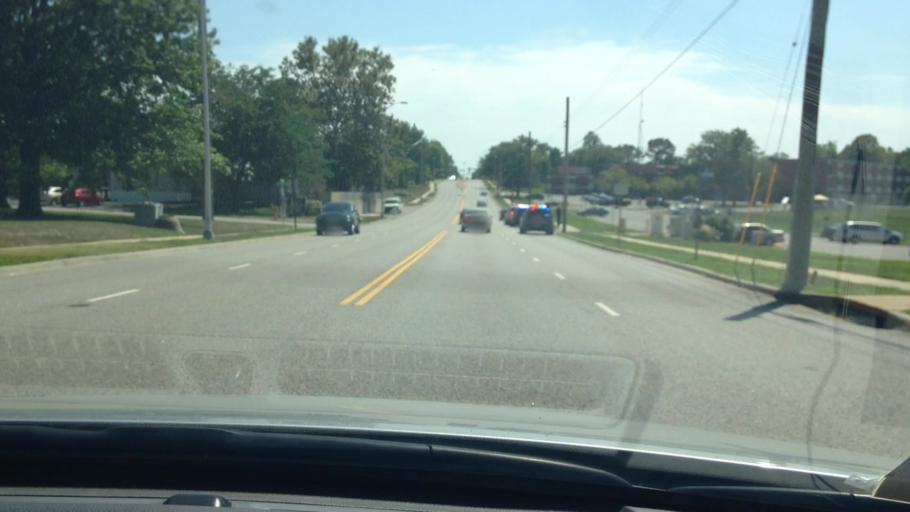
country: US
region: Kansas
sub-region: Johnson County
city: Overland Park
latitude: 38.9786
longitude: -94.6864
